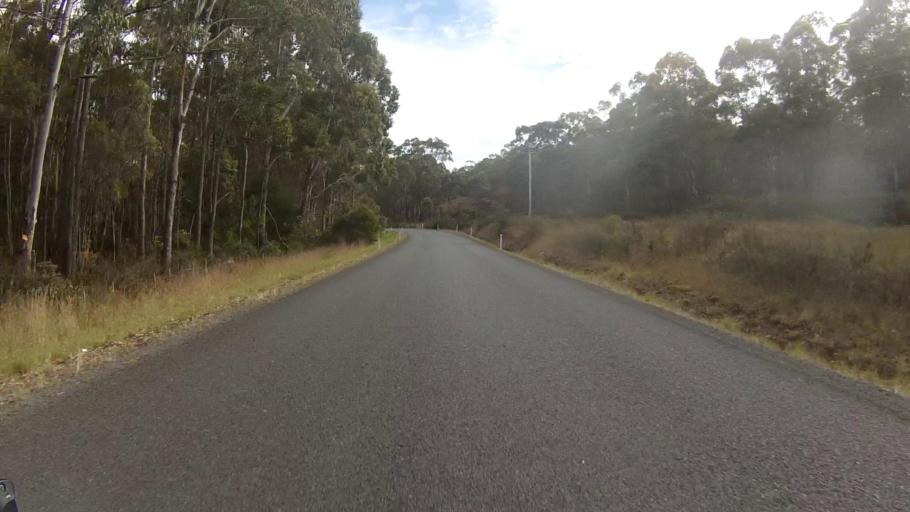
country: AU
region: Tasmania
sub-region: Sorell
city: Sorell
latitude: -42.8151
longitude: 147.7918
